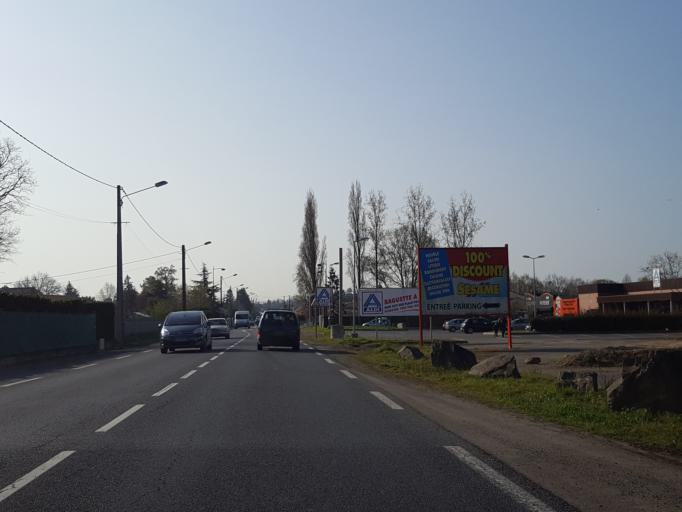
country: FR
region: Pays de la Loire
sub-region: Departement de la Loire-Atlantique
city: Geneston
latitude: 47.0635
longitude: -1.5168
